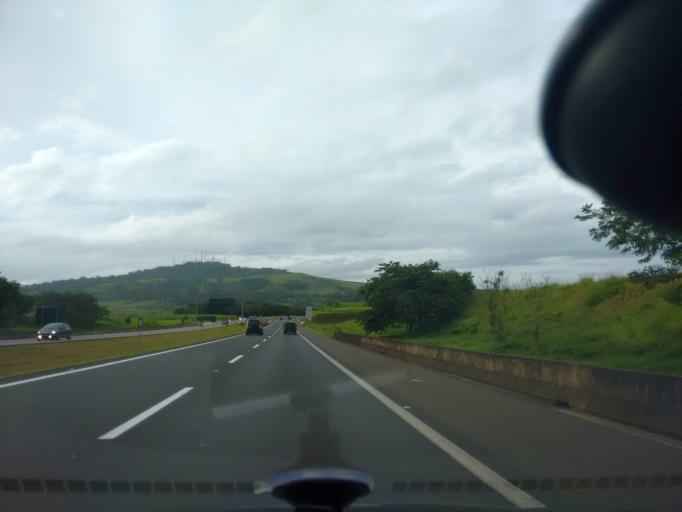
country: BR
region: Sao Paulo
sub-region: Limeira
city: Limeira
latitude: -22.5525
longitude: -47.4612
